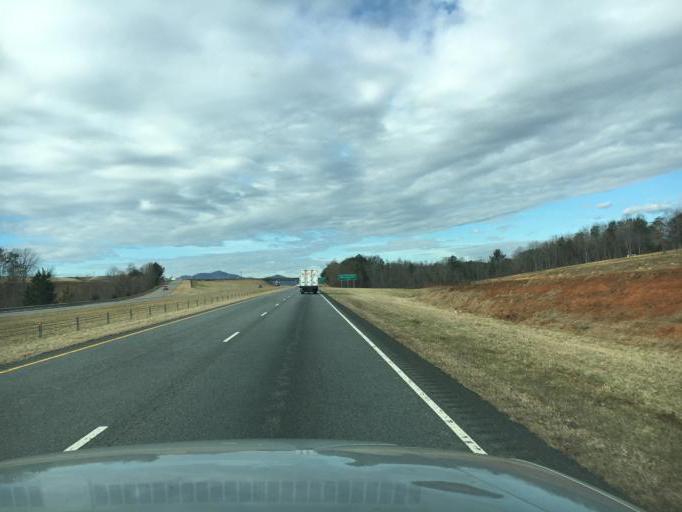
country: US
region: North Carolina
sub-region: Rutherford County
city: Rutherfordton
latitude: 35.2863
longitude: -82.0606
